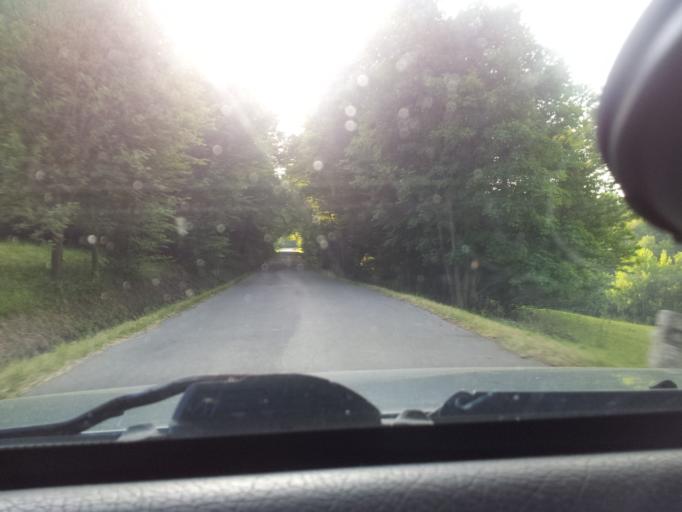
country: SK
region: Banskobystricky
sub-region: Okres Banska Bystrica
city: Banska Stiavnica
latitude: 48.4229
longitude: 18.8599
